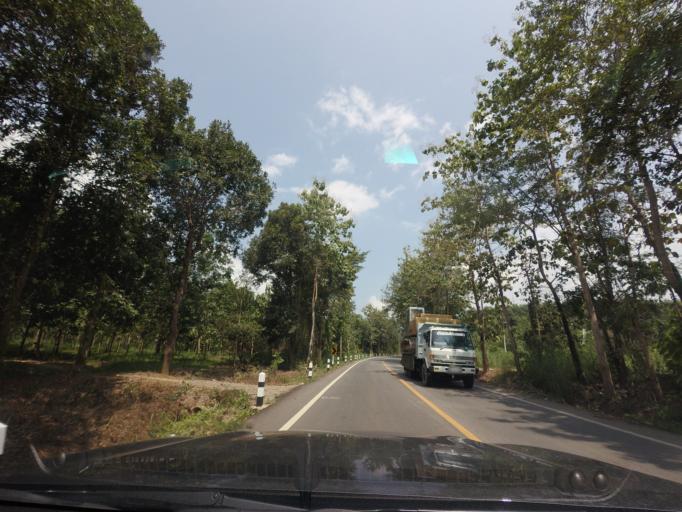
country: TH
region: Nan
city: Santi Suk
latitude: 18.9732
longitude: 100.9283
